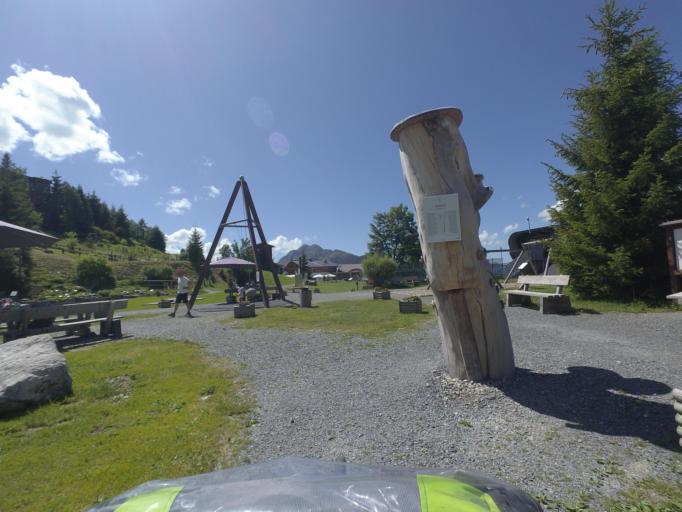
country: AT
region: Salzburg
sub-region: Politischer Bezirk Zell am See
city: Leogang
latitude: 47.4274
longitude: 12.7141
